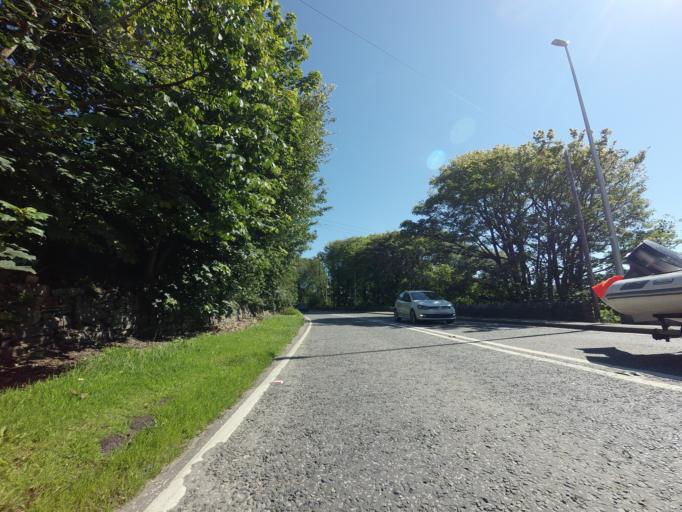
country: GB
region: Scotland
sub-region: Aberdeenshire
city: Macduff
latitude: 57.6598
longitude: -2.5115
